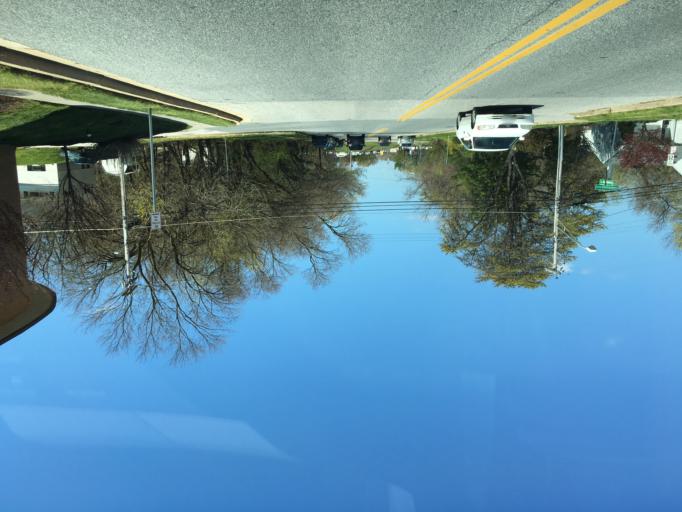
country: US
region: Maryland
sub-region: Baltimore County
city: Timonium
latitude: 39.4578
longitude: -76.6298
